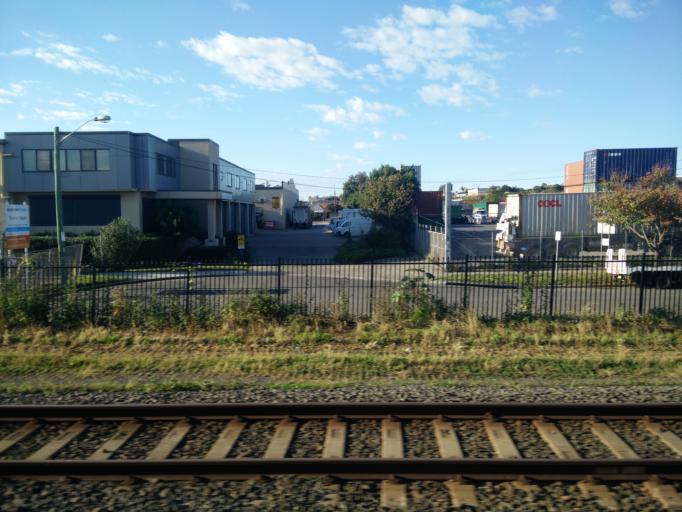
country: AU
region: New South Wales
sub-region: Marrickville
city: Newtown
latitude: -33.9131
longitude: 151.1687
